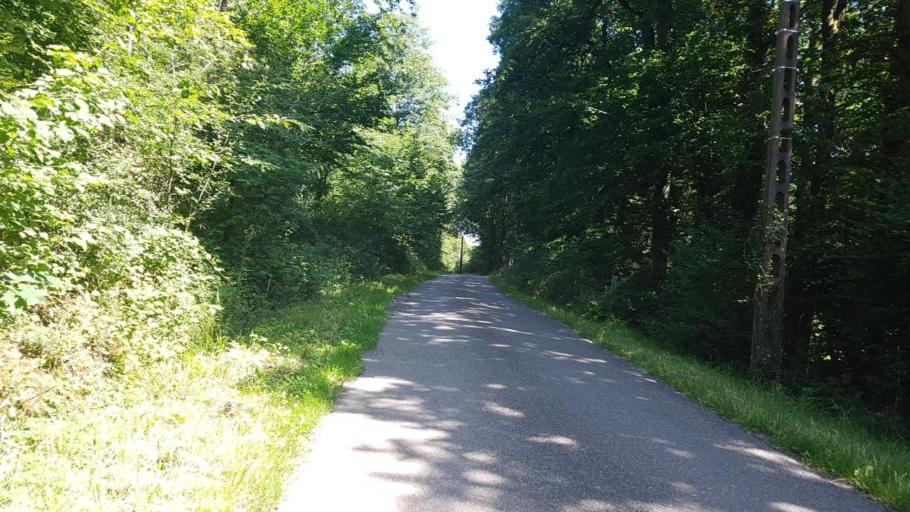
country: BE
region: Wallonia
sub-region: Province du Hainaut
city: Momignies
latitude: 50.1043
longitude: 4.2304
